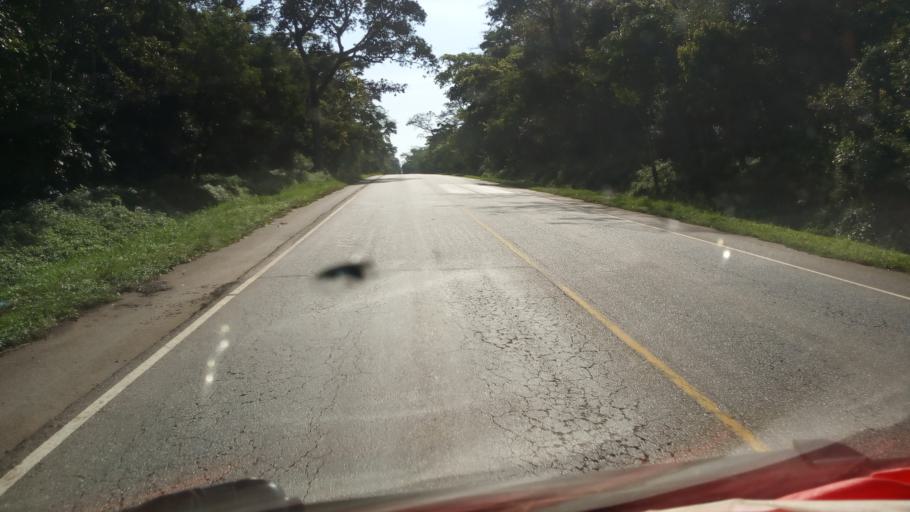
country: UG
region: Eastern Region
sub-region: Busia District
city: Busia
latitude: 0.5374
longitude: 34.0030
